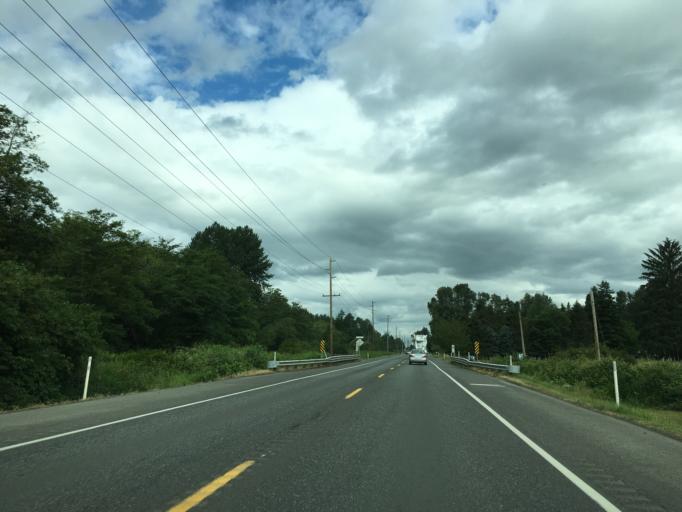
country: US
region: Washington
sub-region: Whatcom County
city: Nooksack
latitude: 48.8394
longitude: -122.2564
